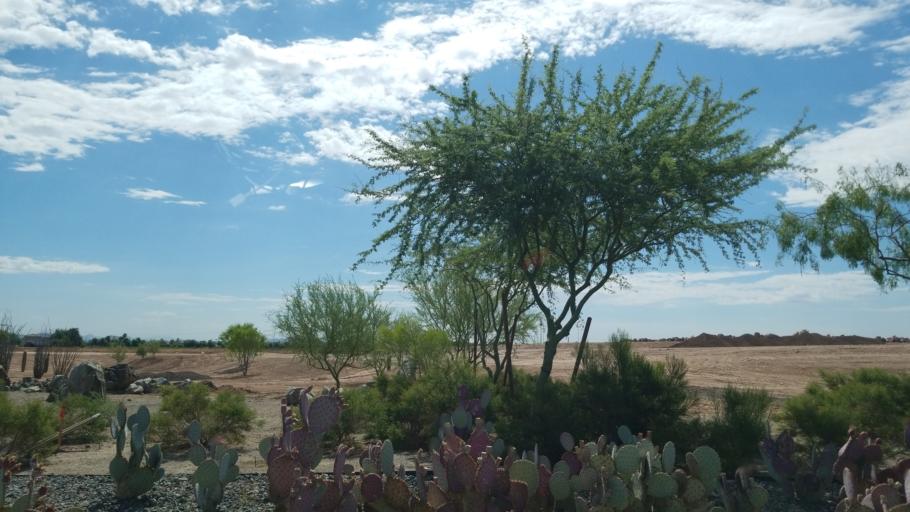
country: US
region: Arizona
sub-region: Maricopa County
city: Peoria
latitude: 33.5497
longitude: -112.2599
